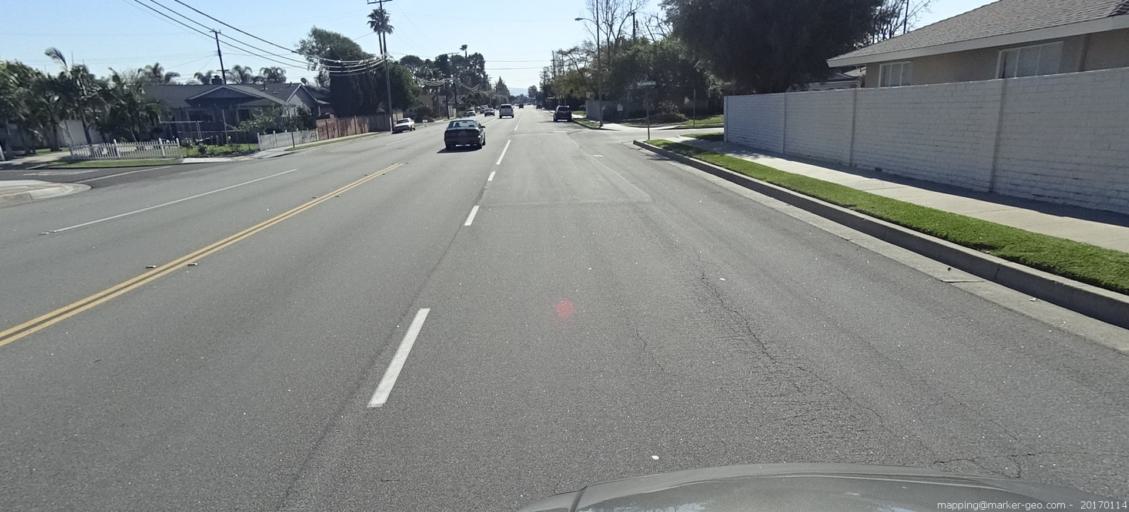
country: US
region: California
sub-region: Orange County
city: Tustin
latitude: 33.7568
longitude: -117.8225
